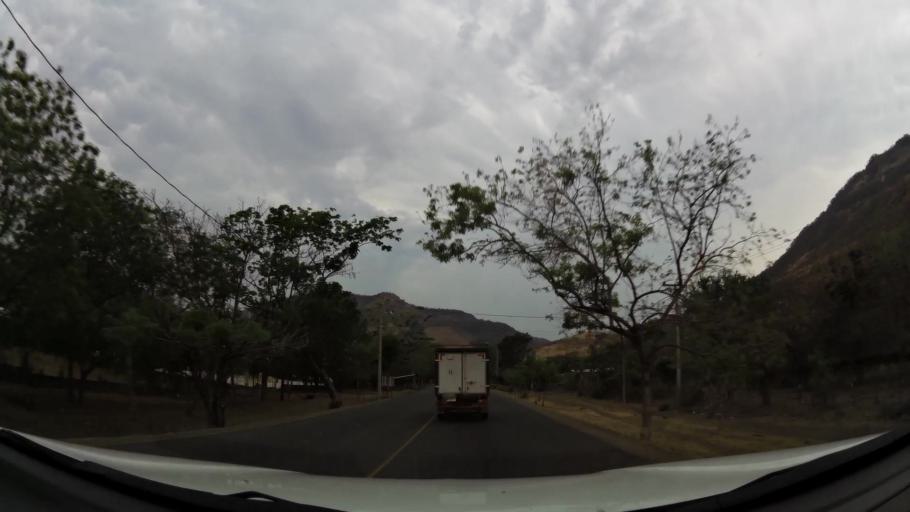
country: NI
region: Leon
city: Santa Rosa del Penon
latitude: 12.9367
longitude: -86.2040
